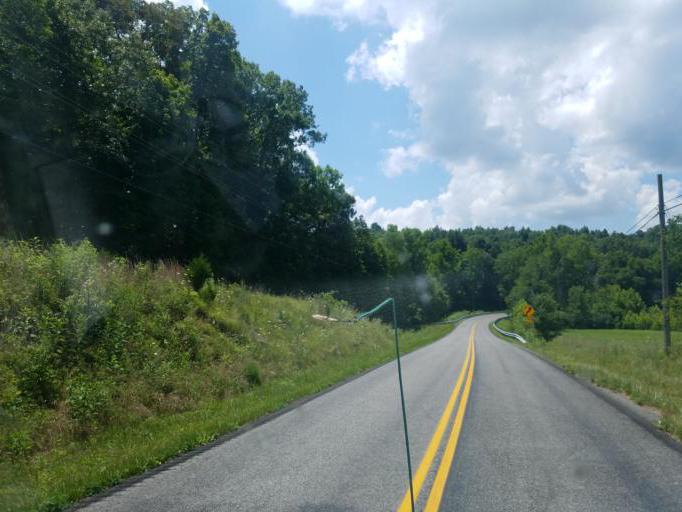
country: US
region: Kentucky
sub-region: Grayson County
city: Leitchfield
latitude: 37.5048
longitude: -86.4720
